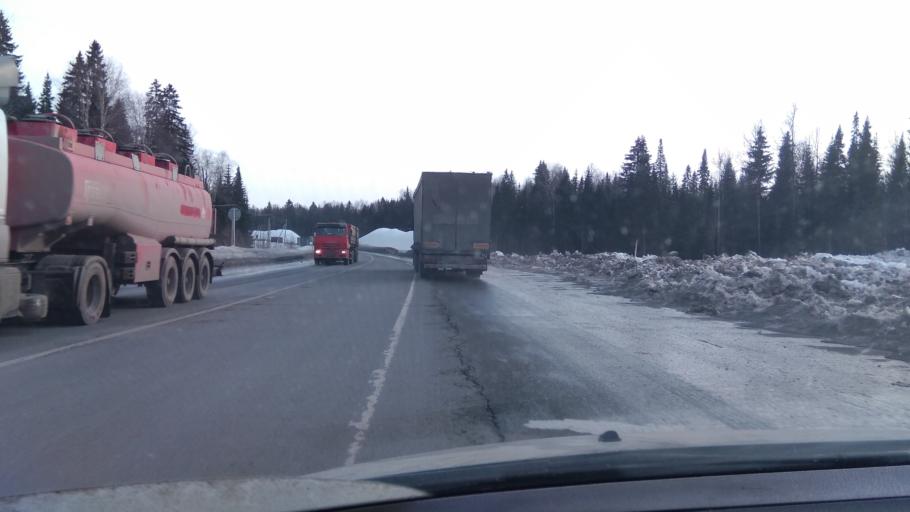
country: RU
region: Perm
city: Ferma
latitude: 57.9933
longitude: 56.3818
